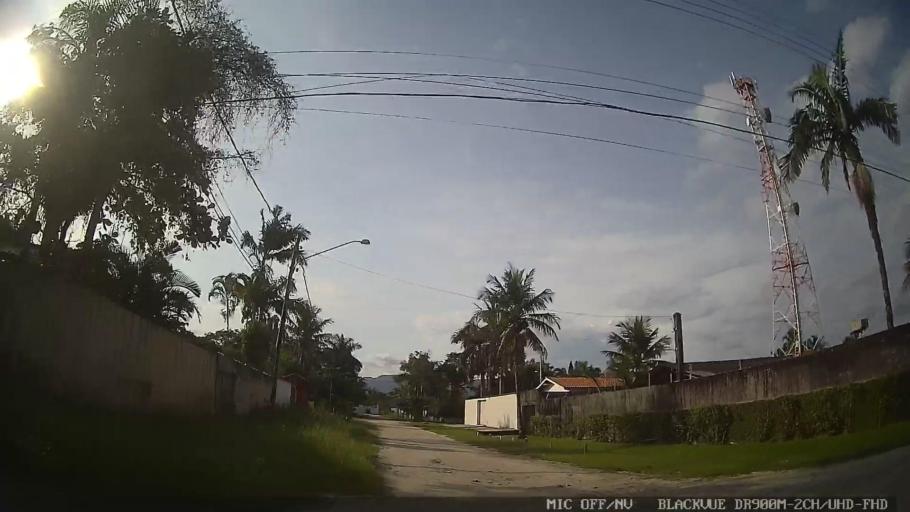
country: BR
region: Sao Paulo
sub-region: Bertioga
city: Bertioga
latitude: -23.8170
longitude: -46.0434
